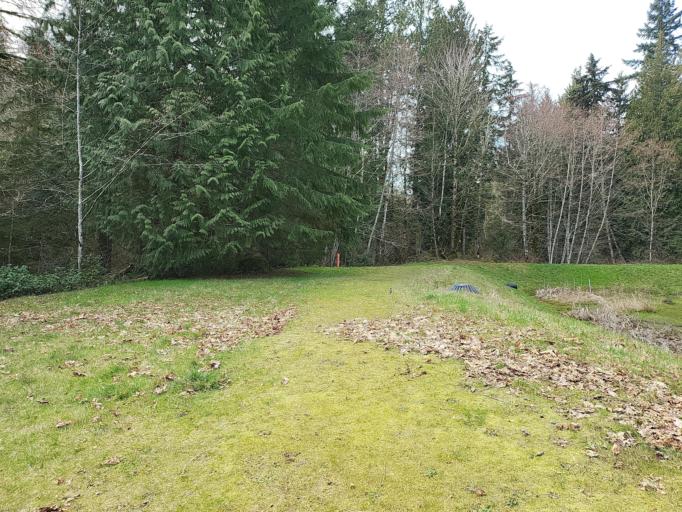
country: US
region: Washington
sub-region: King County
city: East Renton Highlands
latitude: 47.5129
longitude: -122.1190
